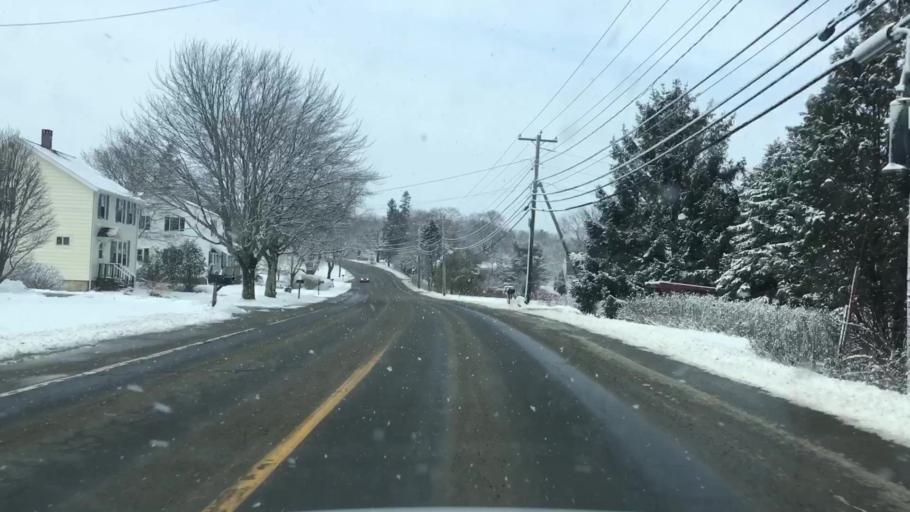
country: US
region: Maine
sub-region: Knox County
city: Rockland
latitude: 44.0835
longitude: -69.1056
